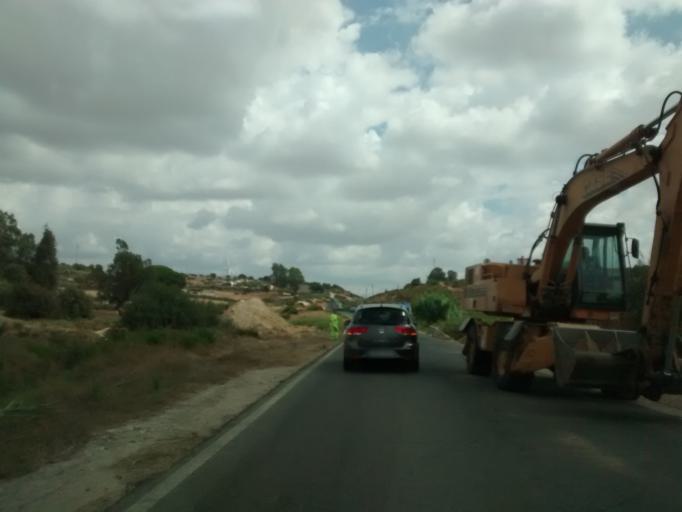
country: ES
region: Andalusia
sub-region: Provincia de Cadiz
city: Medina Sidonia
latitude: 36.4909
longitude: -5.8988
